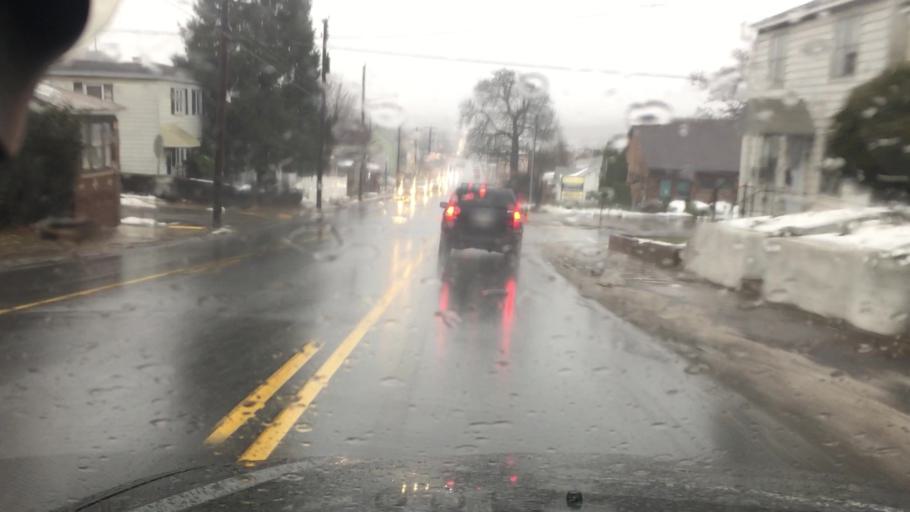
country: US
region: Pennsylvania
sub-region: Luzerne County
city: Harleigh
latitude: 40.9711
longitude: -75.9774
